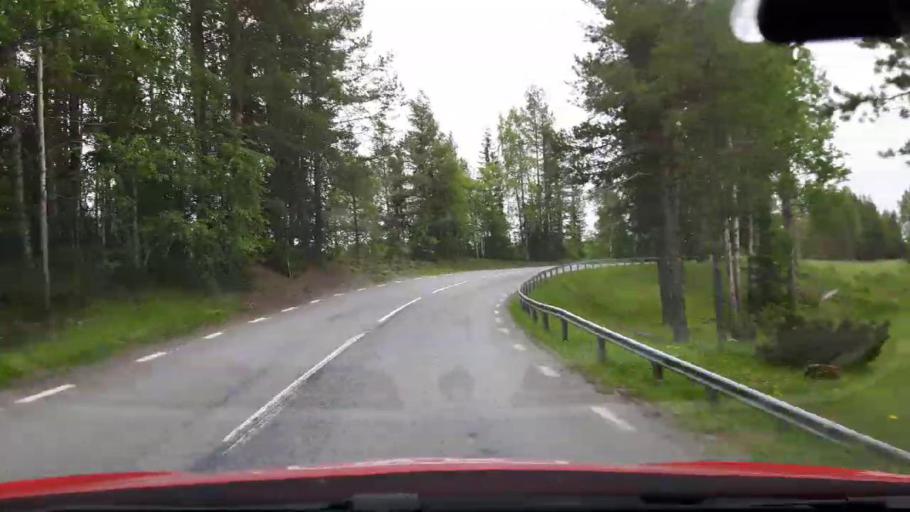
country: SE
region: Jaemtland
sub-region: Stroemsunds Kommun
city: Stroemsund
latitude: 63.5282
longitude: 15.4563
